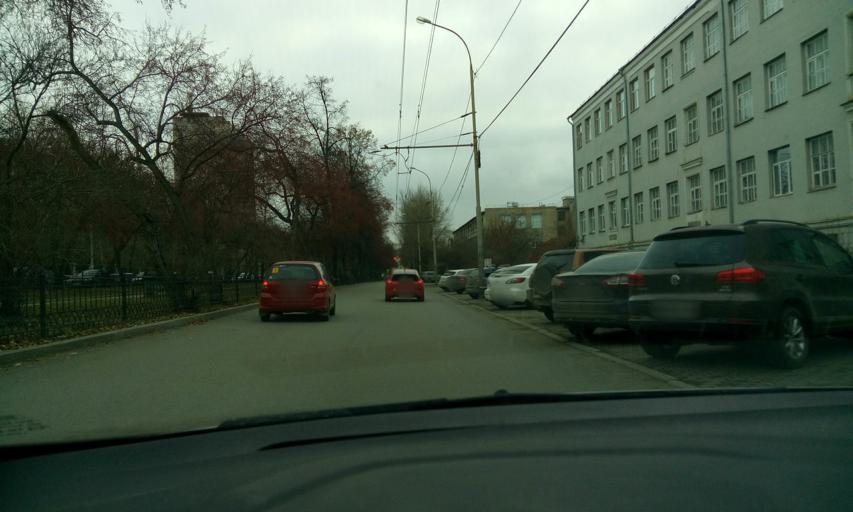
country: RU
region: Sverdlovsk
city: Yekaterinburg
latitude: 56.8427
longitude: 60.6506
